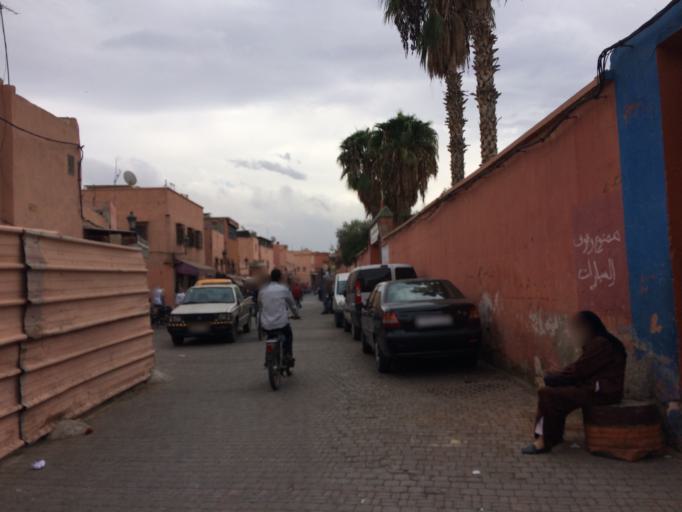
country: MA
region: Marrakech-Tensift-Al Haouz
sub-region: Marrakech
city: Marrakesh
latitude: 31.6352
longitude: -7.9913
